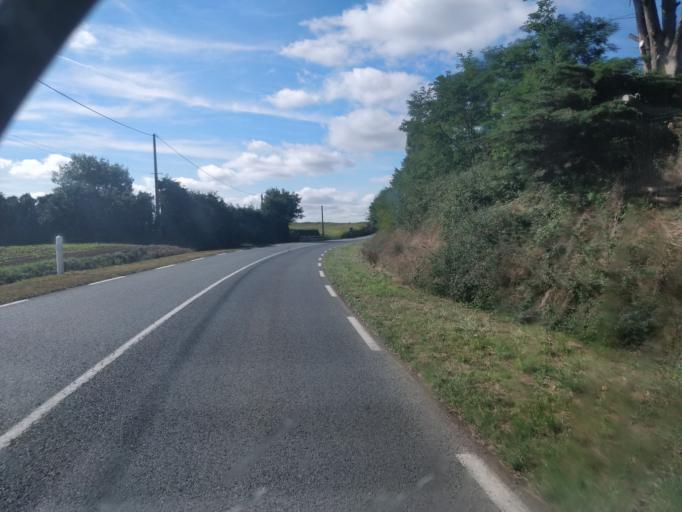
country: FR
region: Brittany
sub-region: Departement des Cotes-d'Armor
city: Erquy
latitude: 48.6106
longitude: -2.4661
